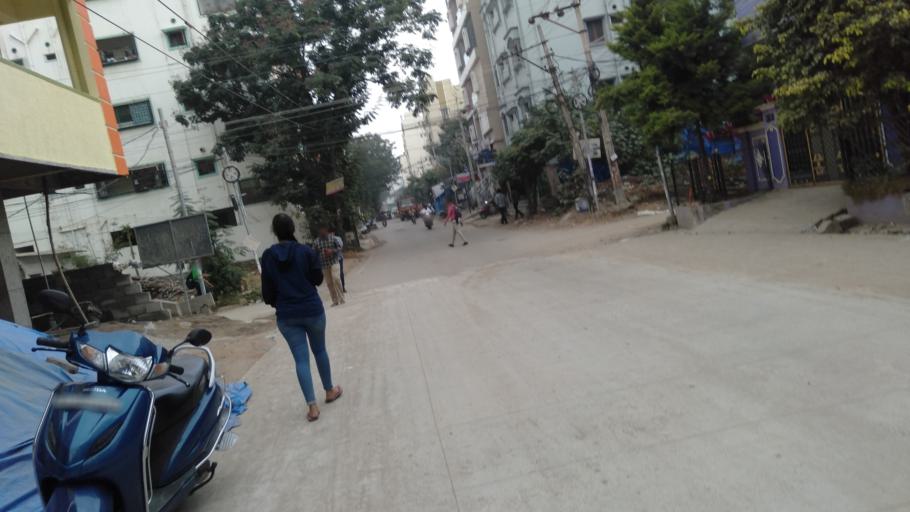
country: IN
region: Telangana
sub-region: Rangareddi
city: Kukatpalli
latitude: 17.4943
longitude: 78.3885
